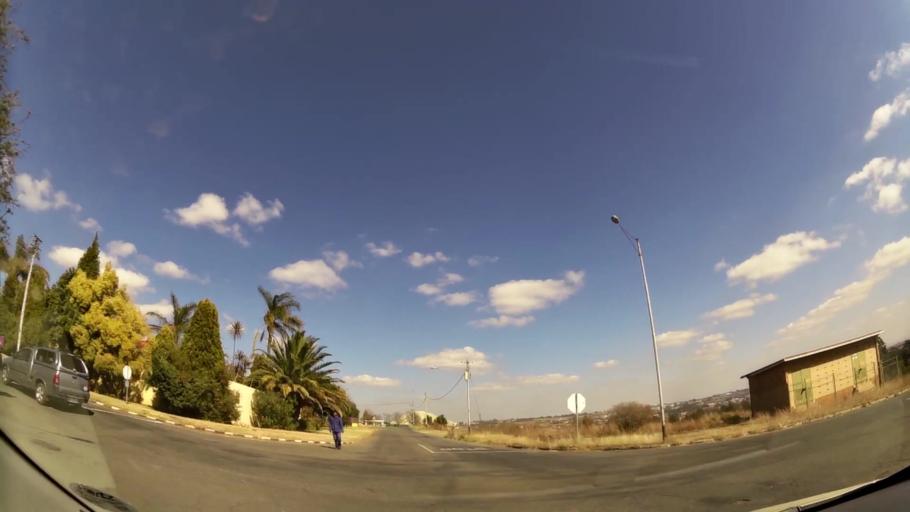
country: ZA
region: Gauteng
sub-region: West Rand District Municipality
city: Krugersdorp
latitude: -26.0932
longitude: 27.7837
